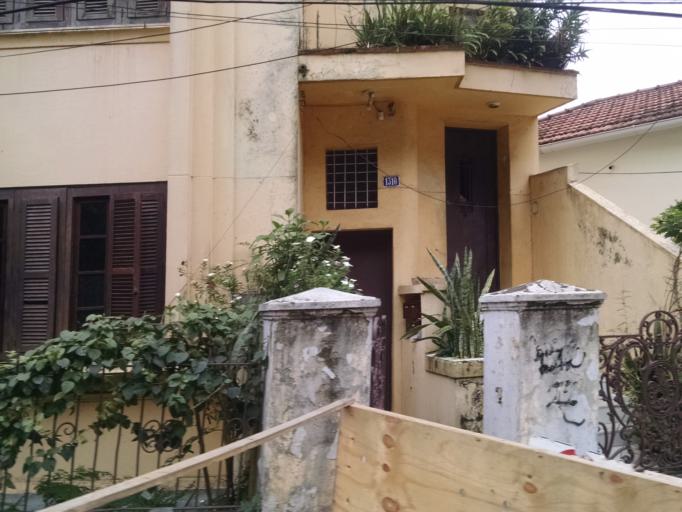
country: BR
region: Rio de Janeiro
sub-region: Rio De Janeiro
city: Rio de Janeiro
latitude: -22.9248
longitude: -43.1895
